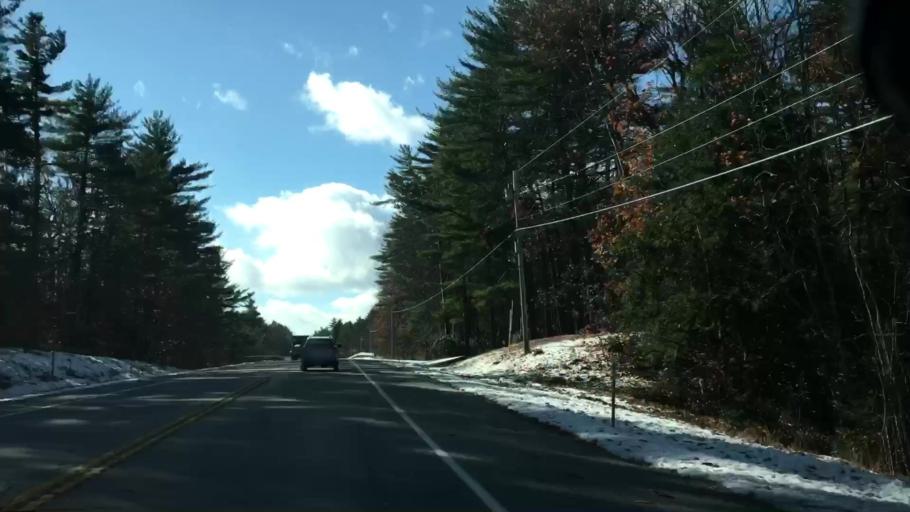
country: US
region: New Hampshire
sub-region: Carroll County
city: Ossipee
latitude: 43.6934
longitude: -71.1159
